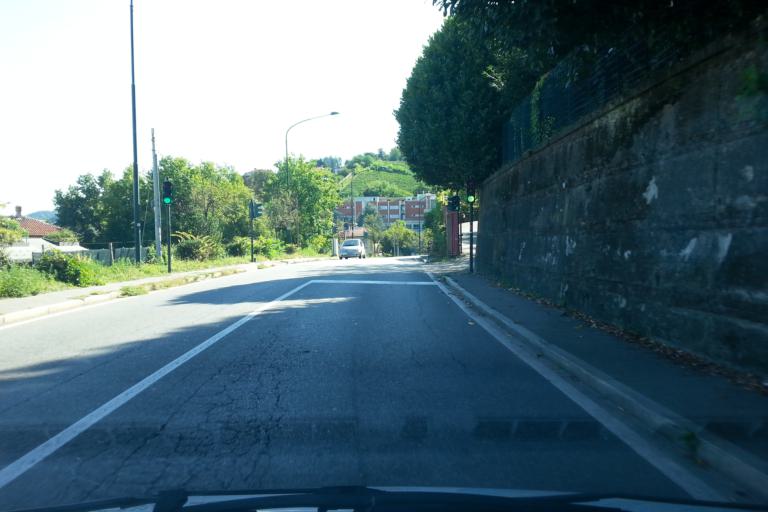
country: IT
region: Piedmont
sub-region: Provincia di Torino
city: Turin
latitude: 45.0596
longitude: 7.7043
